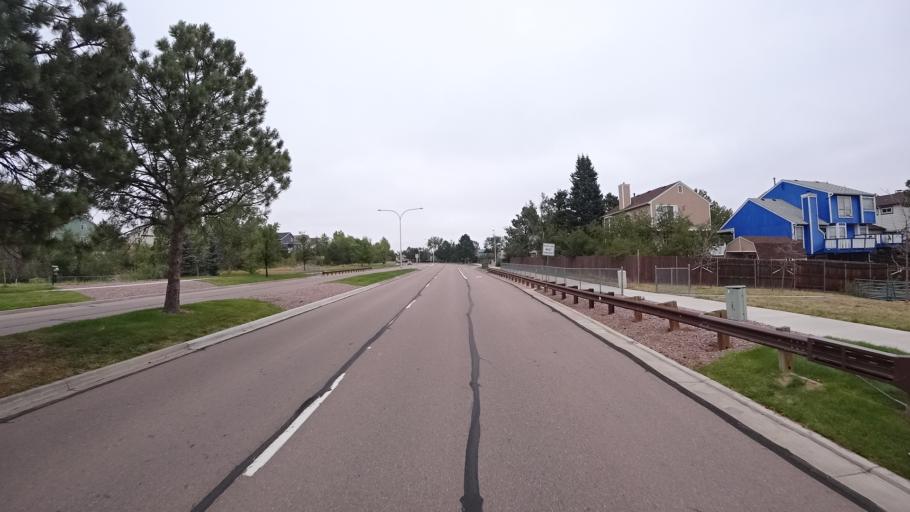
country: US
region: Colorado
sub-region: El Paso County
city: Cimarron Hills
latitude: 38.9028
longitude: -104.7086
